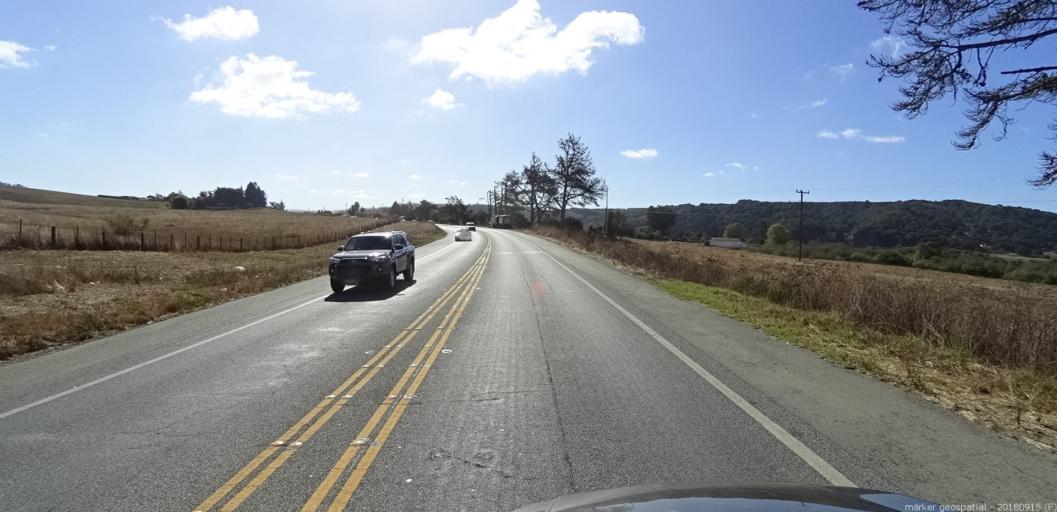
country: US
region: California
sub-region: Monterey County
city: Las Lomas
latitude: 36.8676
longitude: -121.7427
